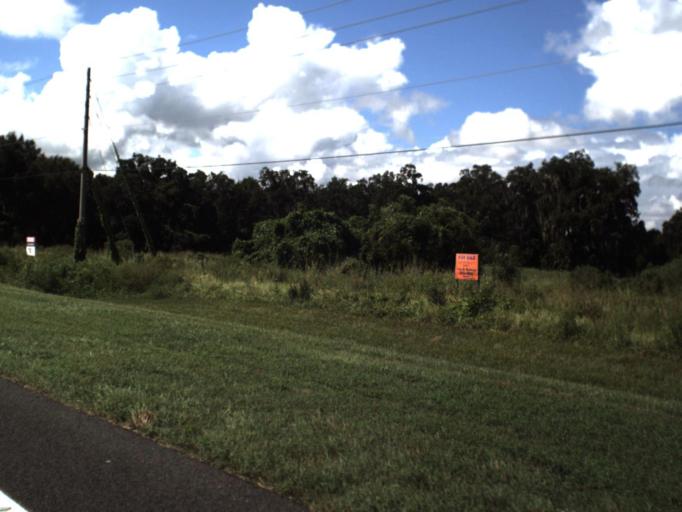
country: US
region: Florida
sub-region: Polk County
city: Medulla
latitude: 27.9422
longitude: -81.9738
